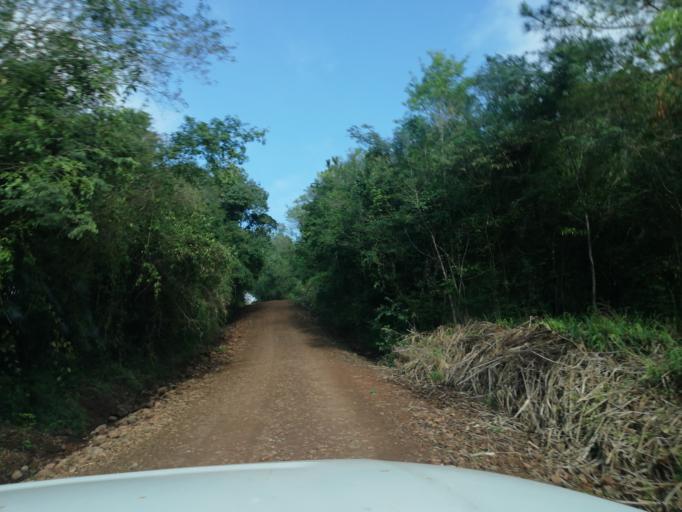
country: AR
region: Misiones
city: Cerro Azul
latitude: -27.5740
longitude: -55.5033
